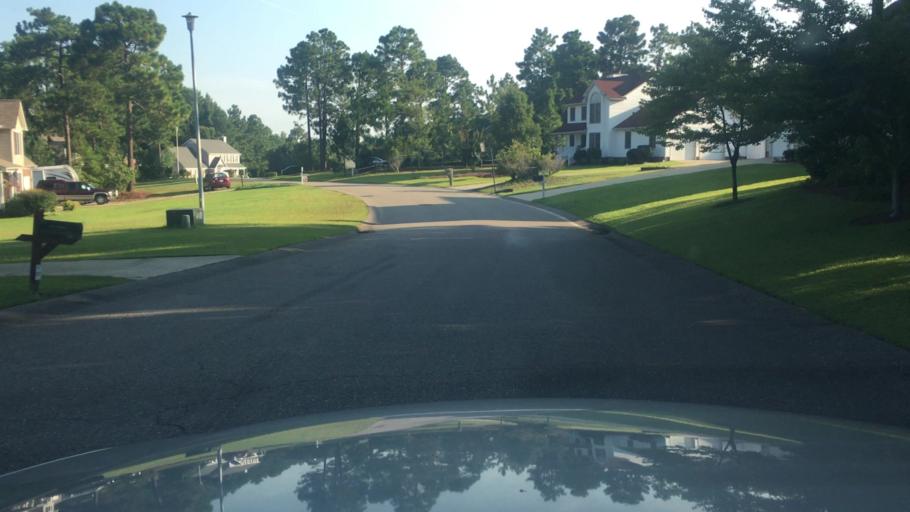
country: US
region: North Carolina
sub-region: Harnett County
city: Walkertown
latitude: 35.2205
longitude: -78.8626
